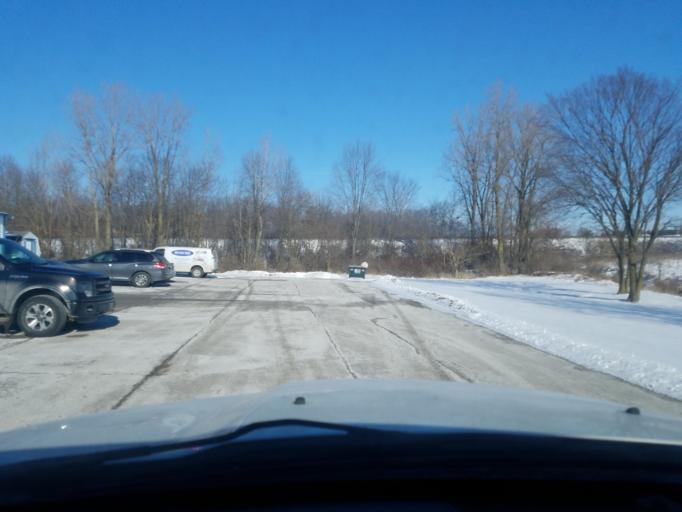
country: US
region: Indiana
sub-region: Noble County
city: Albion
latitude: 41.3892
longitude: -85.4137
